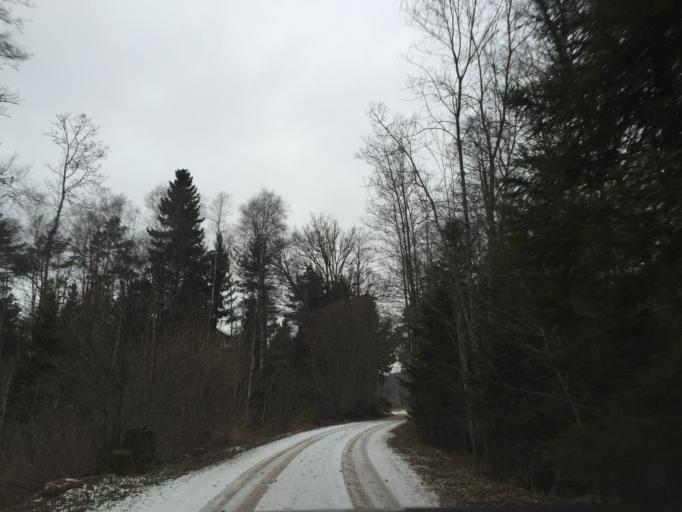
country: EE
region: Saare
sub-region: Kuressaare linn
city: Kuressaare
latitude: 58.3951
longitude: 22.2552
